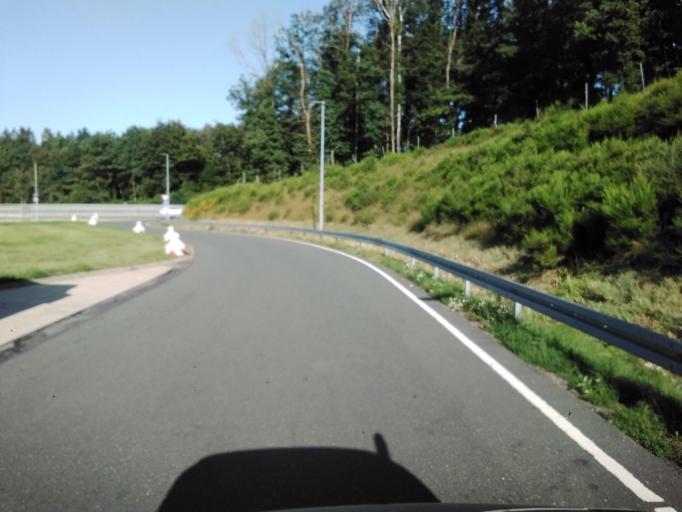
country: DE
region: North Rhine-Westphalia
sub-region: Regierungsbezirk Arnsberg
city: Wenden
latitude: 50.9636
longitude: 7.8456
